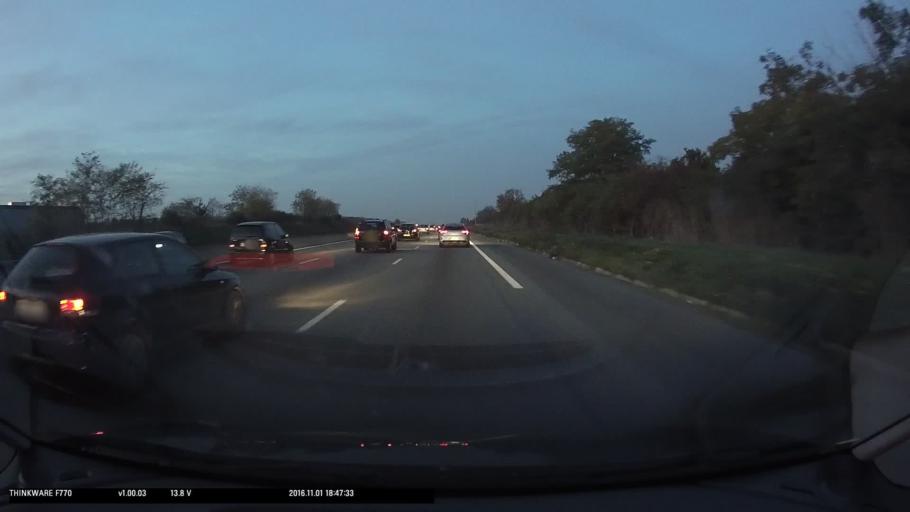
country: FR
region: Ile-de-France
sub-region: Departement de l'Essonne
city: Chilly-Mazarin
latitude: 48.7205
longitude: 2.3112
